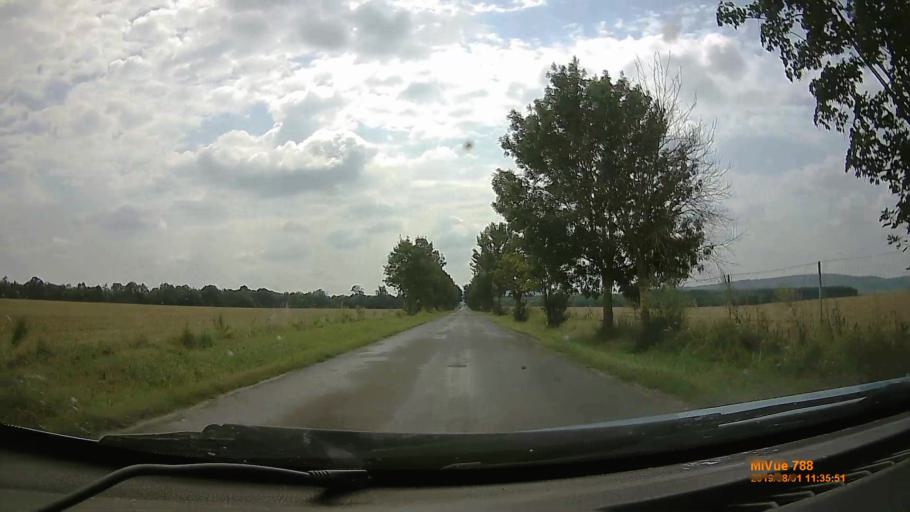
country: HU
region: Baranya
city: Villany
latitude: 45.9232
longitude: 18.3709
